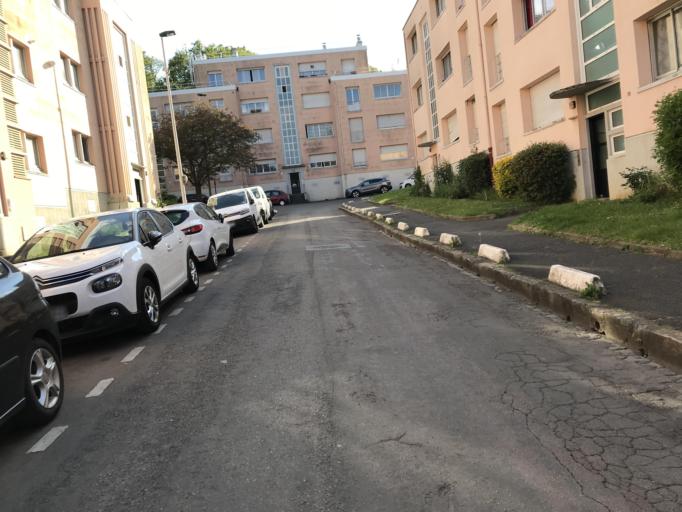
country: FR
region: Ile-de-France
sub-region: Departement des Hauts-de-Seine
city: Chatenay-Malabry
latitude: 48.7622
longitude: 2.2548
